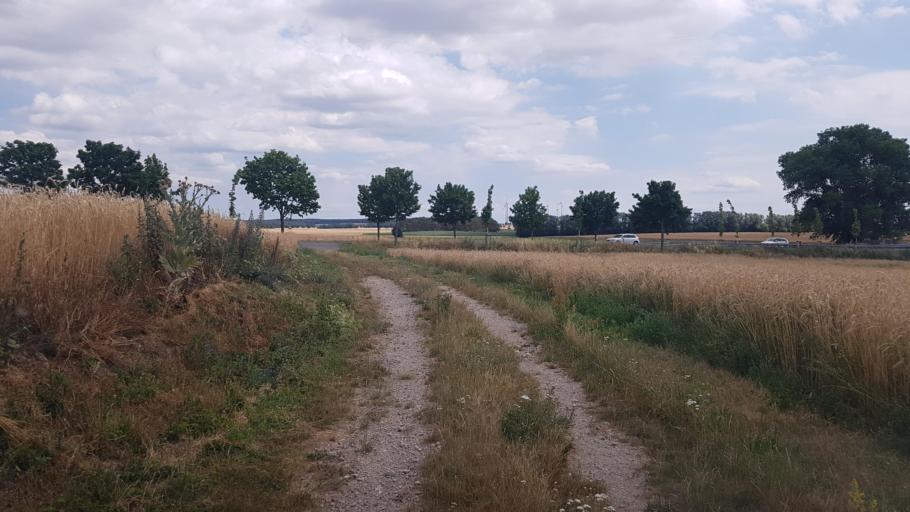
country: DE
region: Brandenburg
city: Juterbog
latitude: 51.9650
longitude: 13.0778
